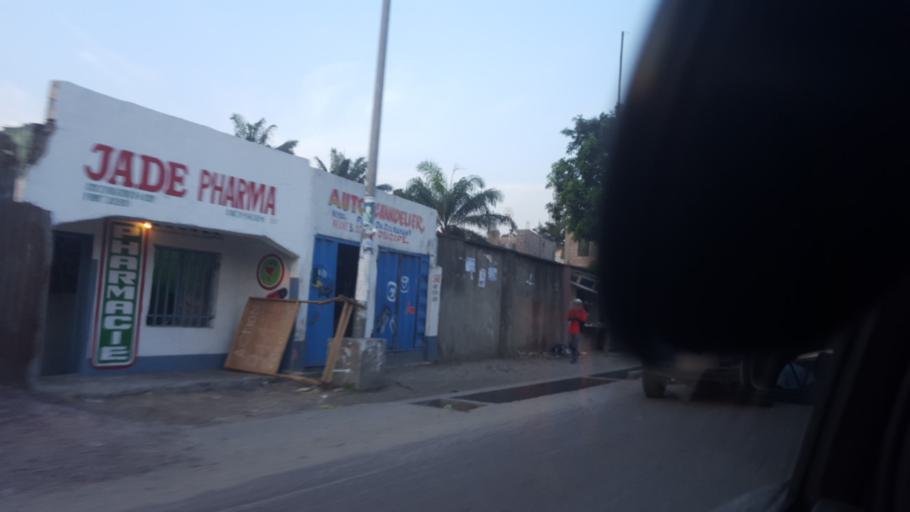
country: CD
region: Kinshasa
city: Kinshasa
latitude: -4.3522
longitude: 15.3278
